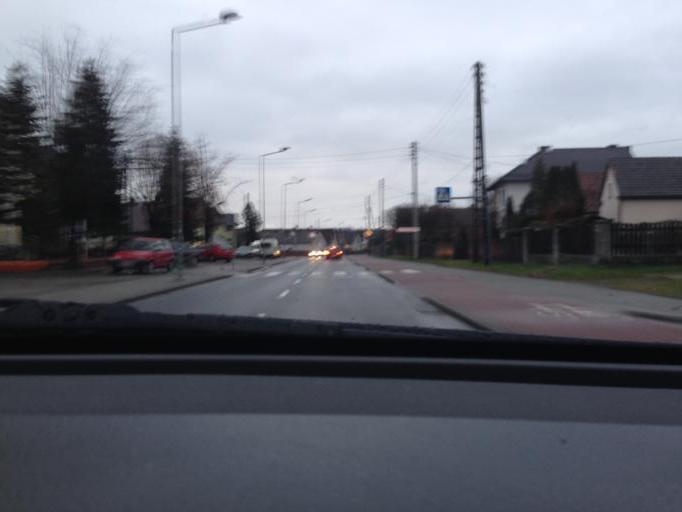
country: PL
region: Opole Voivodeship
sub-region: Powiat opolski
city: Opole
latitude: 50.6815
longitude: 17.9576
